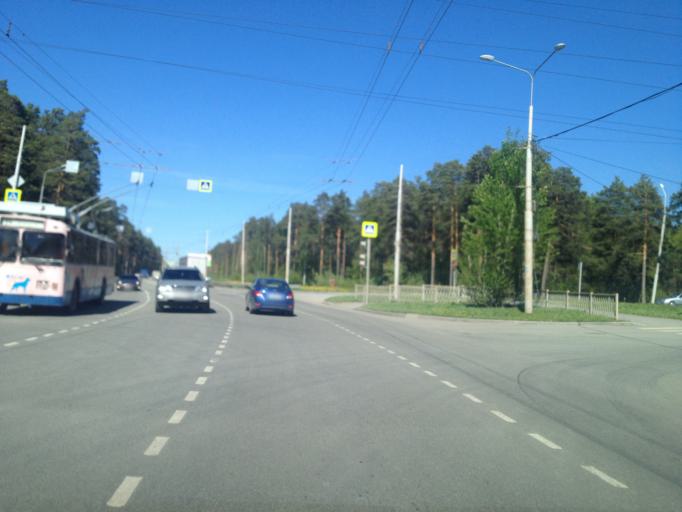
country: RU
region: Sverdlovsk
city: Sovkhoznyy
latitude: 56.7800
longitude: 60.5589
